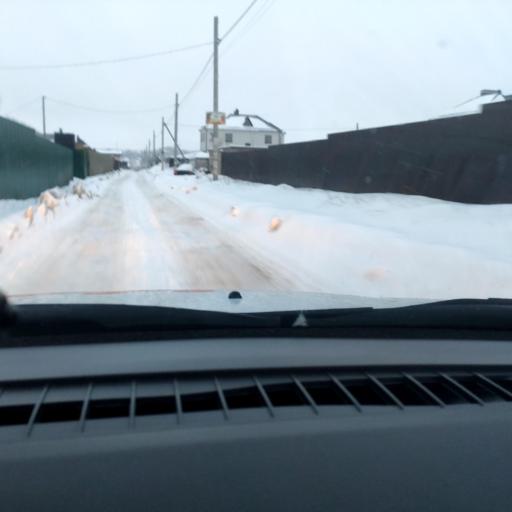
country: RU
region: Samara
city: Dubovyy Umet
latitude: 53.0311
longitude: 50.2285
